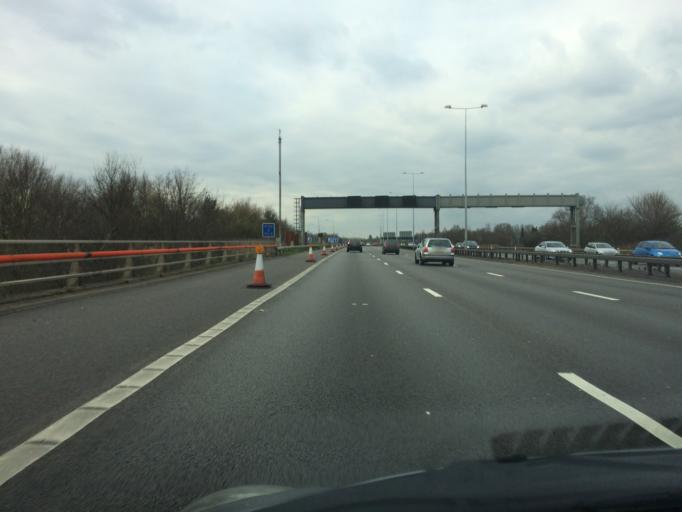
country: GB
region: England
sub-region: Surrey
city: Virginia Water
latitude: 51.4004
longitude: -0.5375
